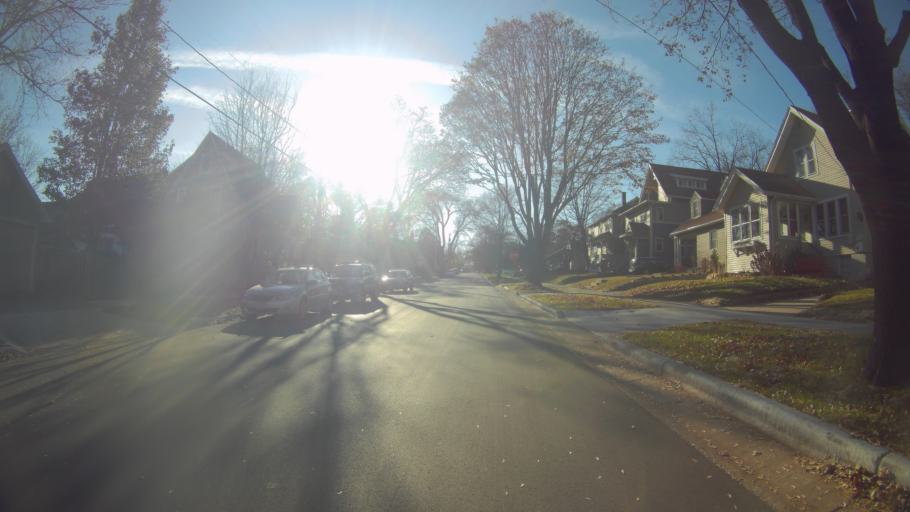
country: US
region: Wisconsin
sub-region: Dane County
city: Shorewood Hills
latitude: 43.0576
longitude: -89.4329
